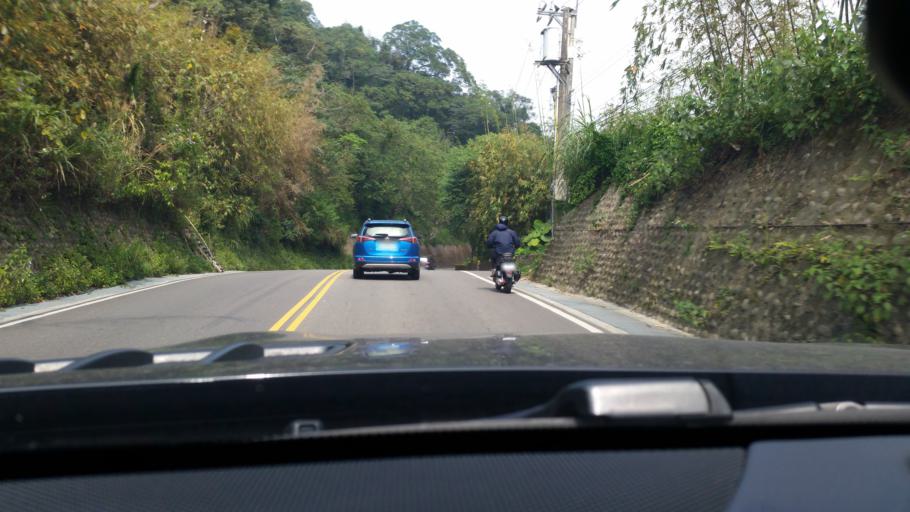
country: TW
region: Taiwan
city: Daxi
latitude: 24.8286
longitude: 121.3162
